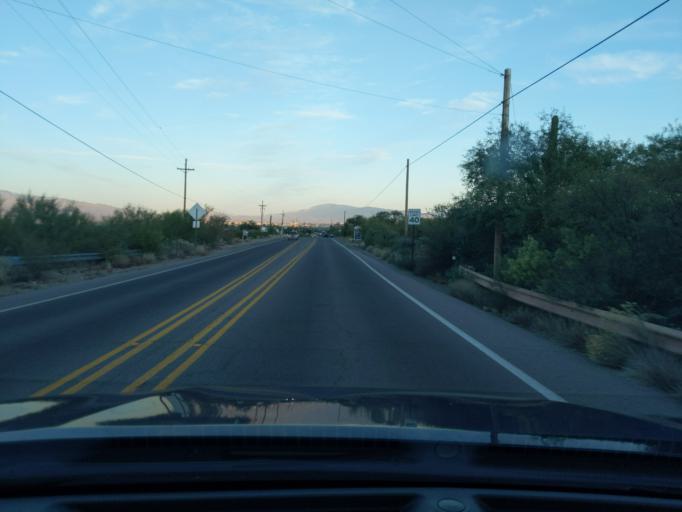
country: US
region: Arizona
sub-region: Pima County
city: Tucson Estates
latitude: 32.2249
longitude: -111.0359
